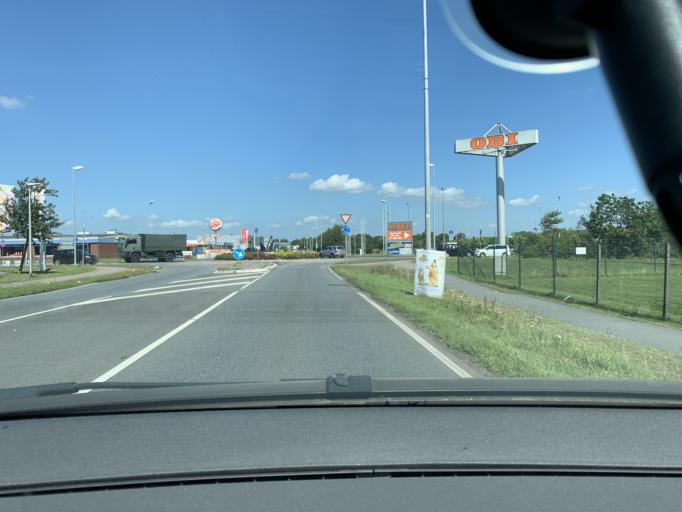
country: DE
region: Schleswig-Holstein
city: Husum
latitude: 54.4892
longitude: 9.0804
